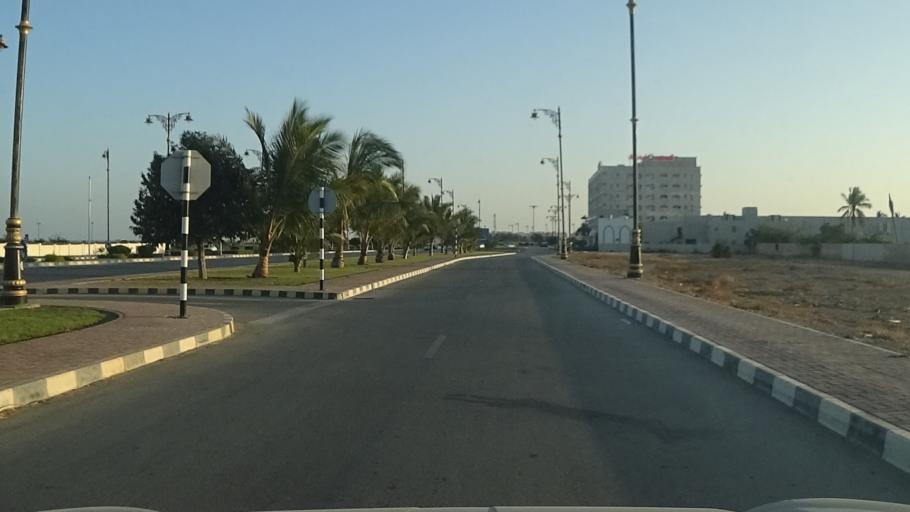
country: OM
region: Zufar
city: Salalah
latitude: 17.0301
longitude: 54.1721
